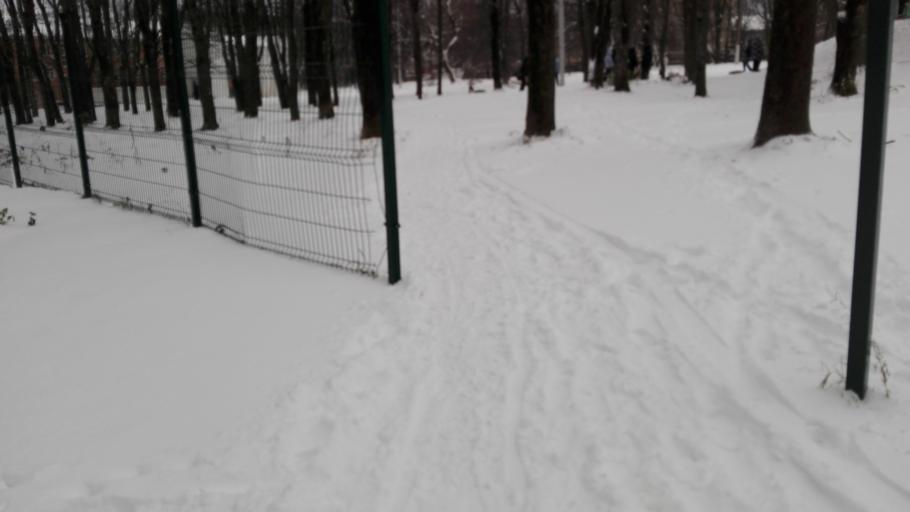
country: RU
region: Tula
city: Kosaya Gora
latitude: 54.1204
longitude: 37.5423
